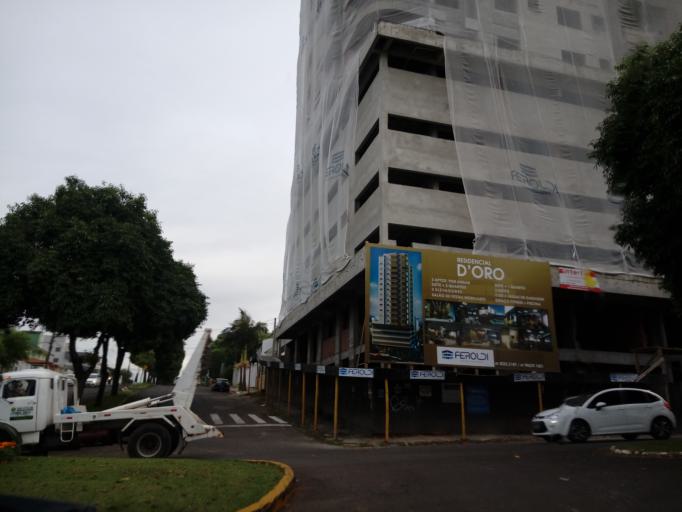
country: BR
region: Santa Catarina
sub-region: Chapeco
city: Chapeco
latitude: -27.0934
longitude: -52.6078
